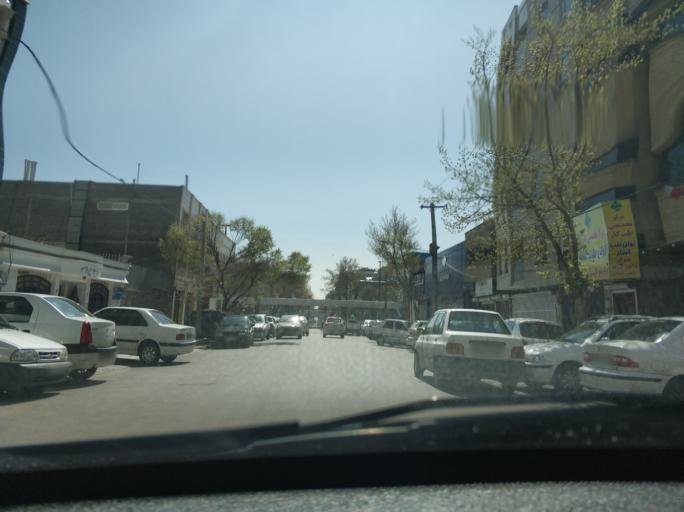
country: IR
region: Razavi Khorasan
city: Mashhad
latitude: 36.2704
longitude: 59.5995
